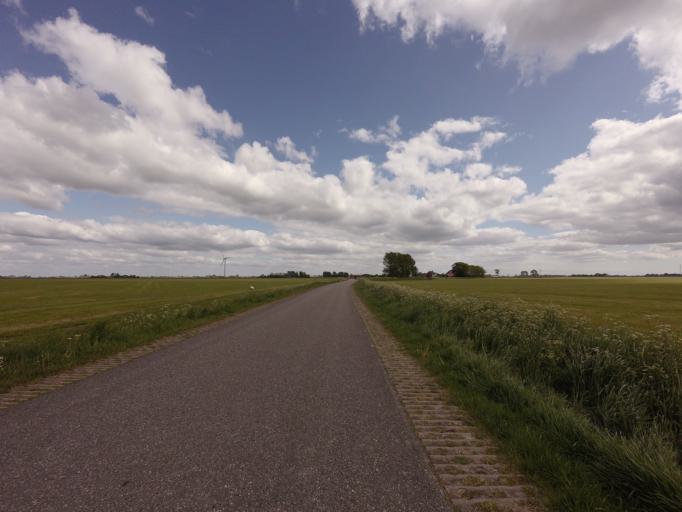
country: NL
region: Friesland
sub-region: Sudwest Fryslan
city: Bolsward
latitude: 53.0827
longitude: 5.5491
